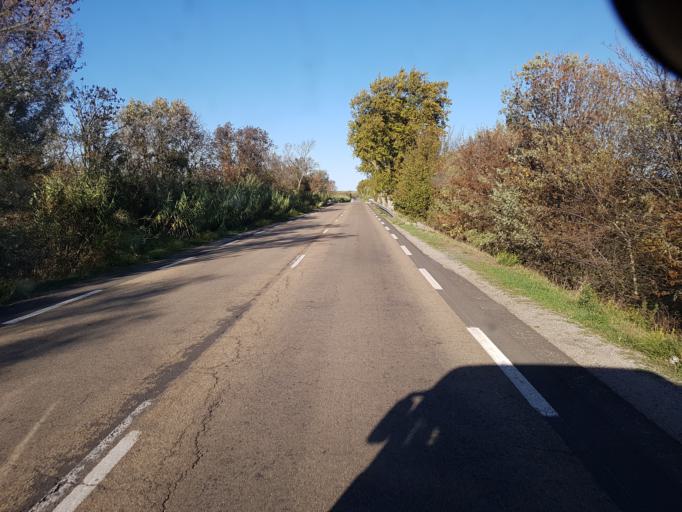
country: FR
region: Languedoc-Roussillon
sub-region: Departement de l'Aude
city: Coursan
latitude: 43.2479
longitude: 3.0668
